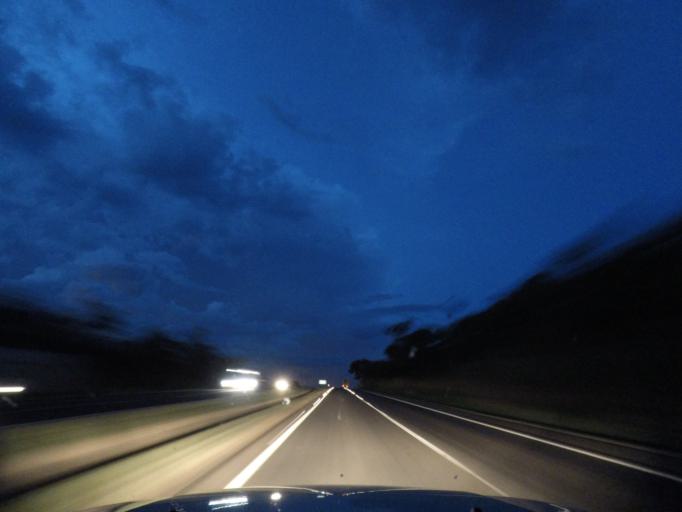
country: BR
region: Minas Gerais
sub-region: Uberlandia
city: Uberlandia
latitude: -19.2285
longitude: -48.1433
